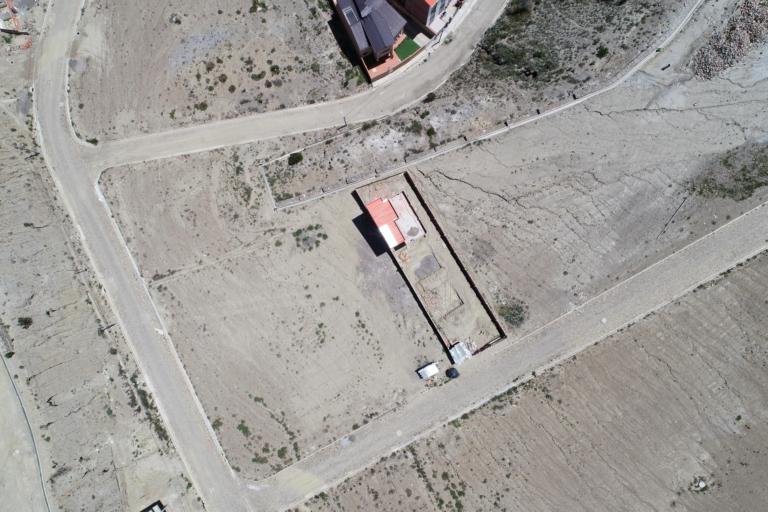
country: BO
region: La Paz
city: La Paz
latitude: -16.5227
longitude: -68.0492
